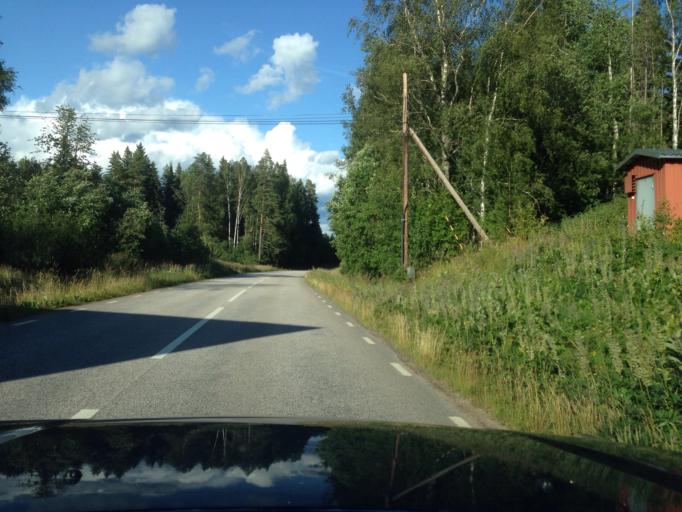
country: SE
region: Dalarna
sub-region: Ludvika Kommun
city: Abborrberget
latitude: 60.2073
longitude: 14.8820
